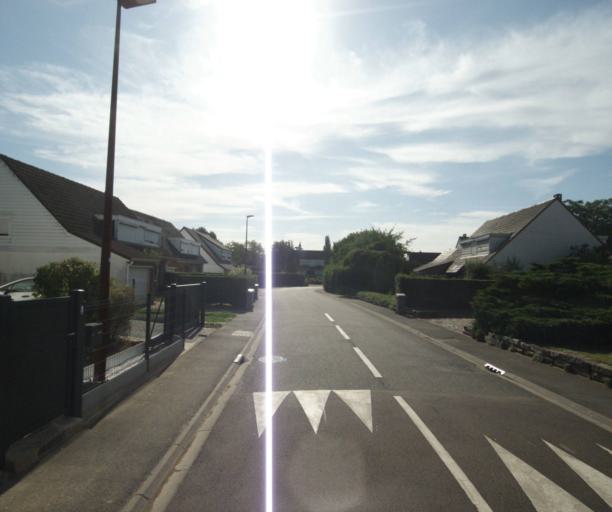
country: FR
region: Nord-Pas-de-Calais
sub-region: Departement du Nord
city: Sainghin-en-Melantois
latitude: 50.5860
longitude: 3.1701
